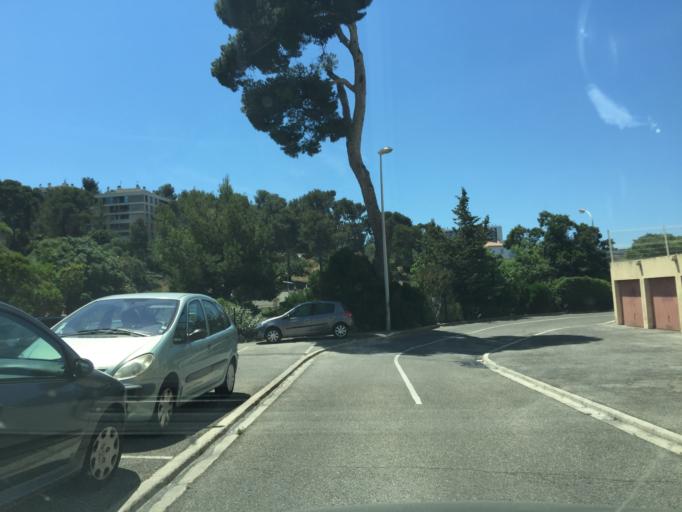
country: FR
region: Provence-Alpes-Cote d'Azur
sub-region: Departement des Bouches-du-Rhone
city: Marseille 09
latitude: 43.2465
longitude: 5.4156
